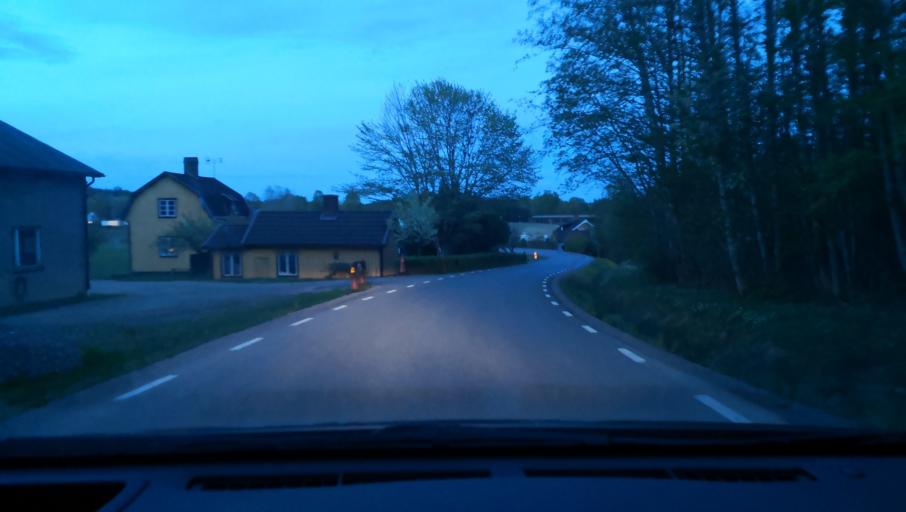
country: SE
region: OErebro
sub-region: Askersunds Kommun
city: Asbro
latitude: 59.0683
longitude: 14.9973
